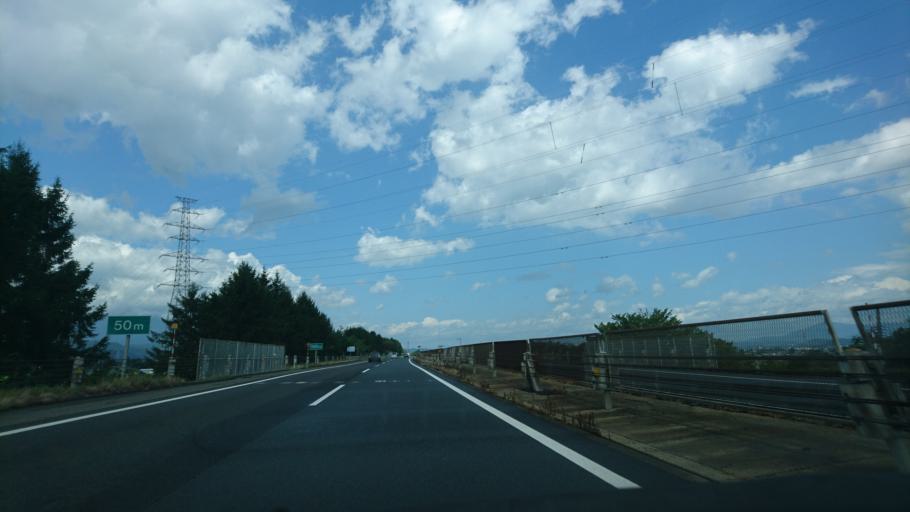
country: JP
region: Iwate
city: Morioka-shi
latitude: 39.6826
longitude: 141.1025
